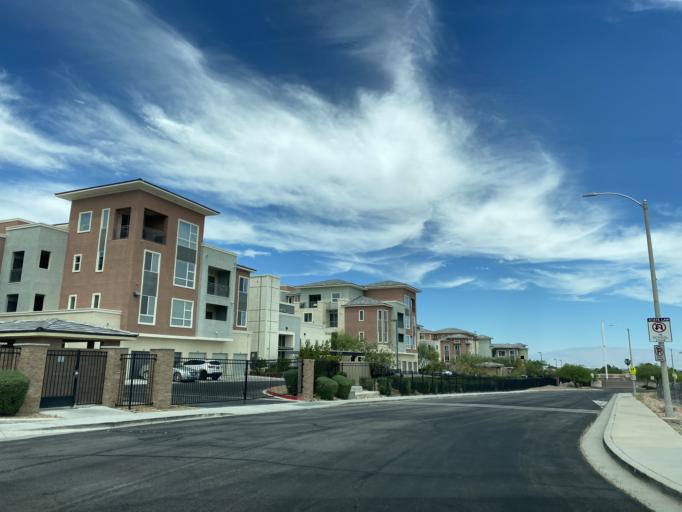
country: US
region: Nevada
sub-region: Clark County
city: Whitney
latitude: 36.0226
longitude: -115.0792
